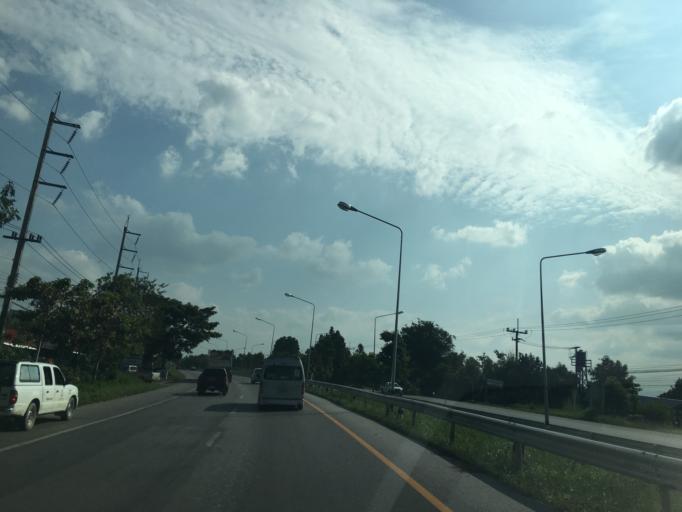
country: TH
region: Chiang Rai
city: Mae Lao
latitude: 19.7047
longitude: 99.7189
